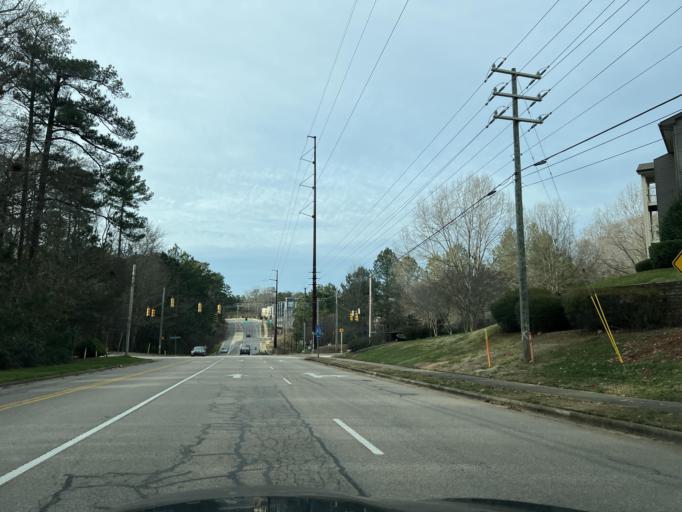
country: US
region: North Carolina
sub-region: Wake County
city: Cary
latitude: 35.8030
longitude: -78.7338
